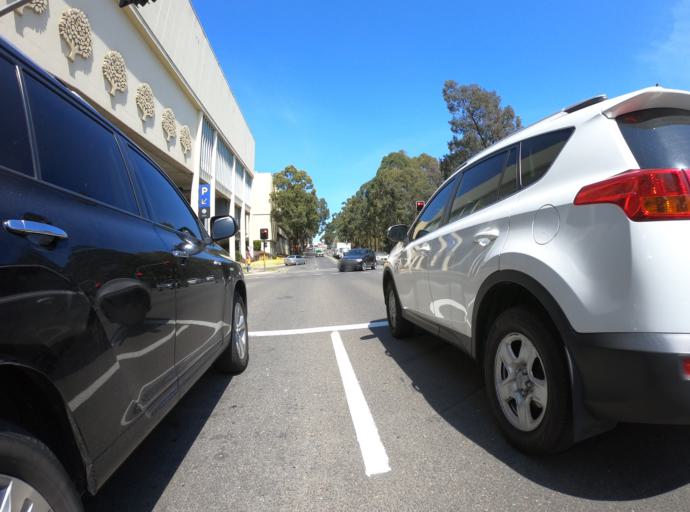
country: AU
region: New South Wales
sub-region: The Hills Shire
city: Castle Hill
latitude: -33.7292
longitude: 151.0059
